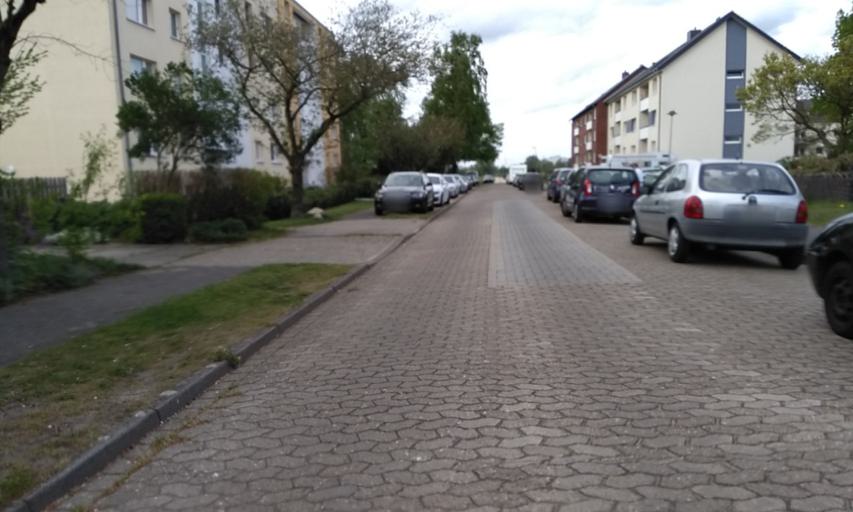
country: DE
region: Lower Saxony
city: Buxtehude
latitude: 53.4751
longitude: 9.6806
